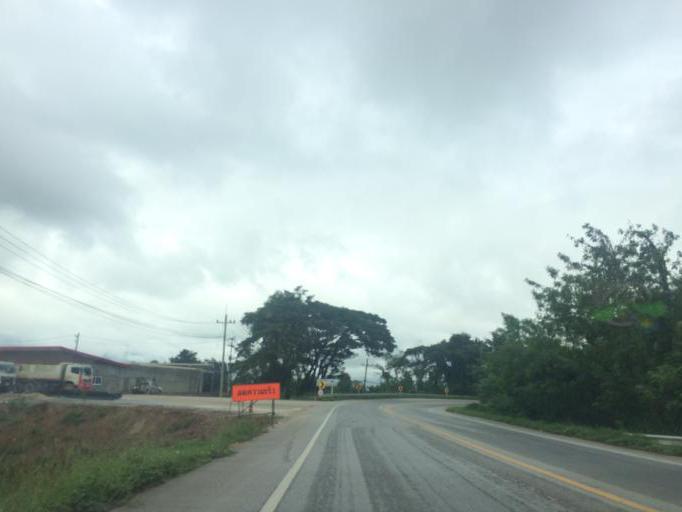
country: TH
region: Chiang Rai
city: Mae Lao
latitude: 19.7465
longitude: 99.6776
